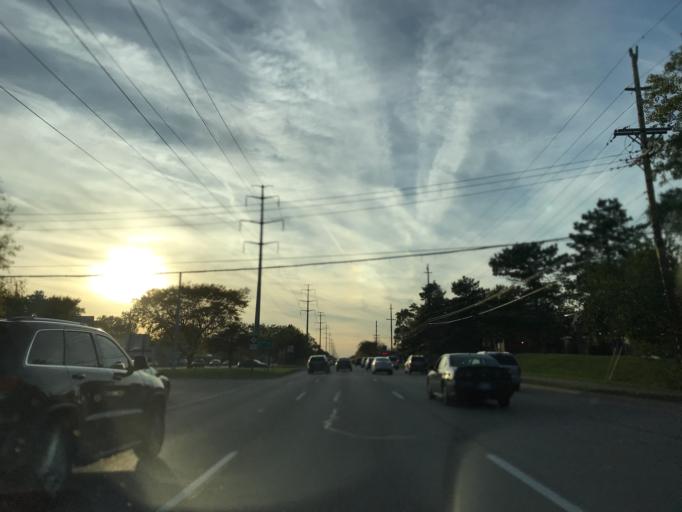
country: US
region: Michigan
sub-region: Wayne County
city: Redford
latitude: 42.4429
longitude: -83.2873
